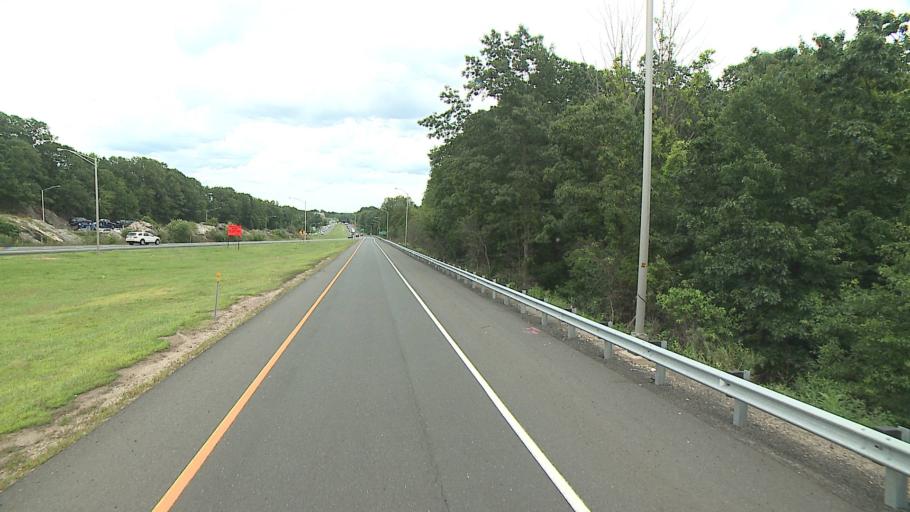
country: US
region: Connecticut
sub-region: New Haven County
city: Waterbury
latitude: 41.5409
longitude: -73.0781
